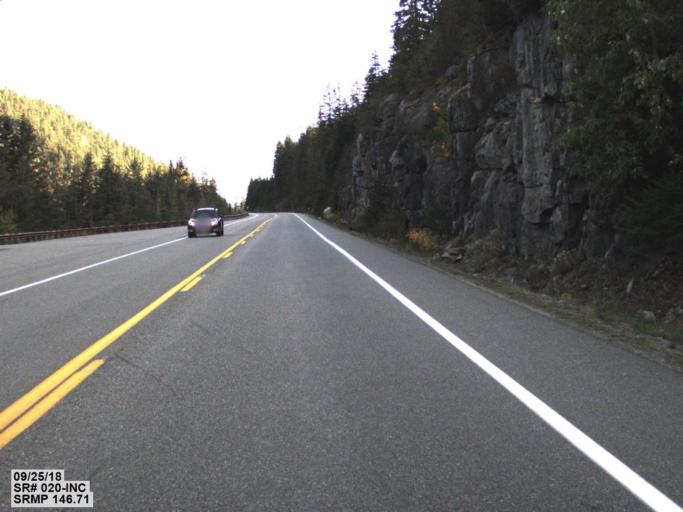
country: US
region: Washington
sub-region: Snohomish County
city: Darrington
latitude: 48.6450
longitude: -120.8553
